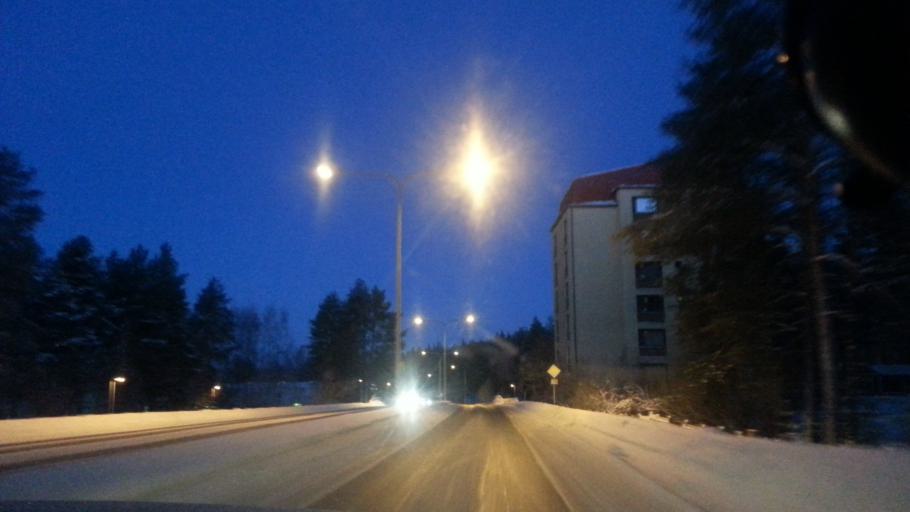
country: FI
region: Lapland
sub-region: Rovaniemi
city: Rovaniemi
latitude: 66.4980
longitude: 25.7566
